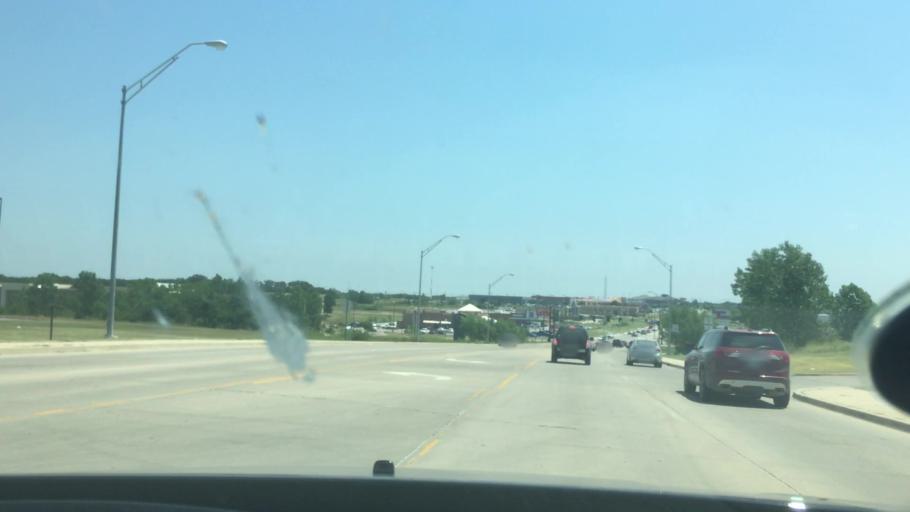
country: US
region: Oklahoma
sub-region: Pontotoc County
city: Ada
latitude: 34.7905
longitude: -96.6631
